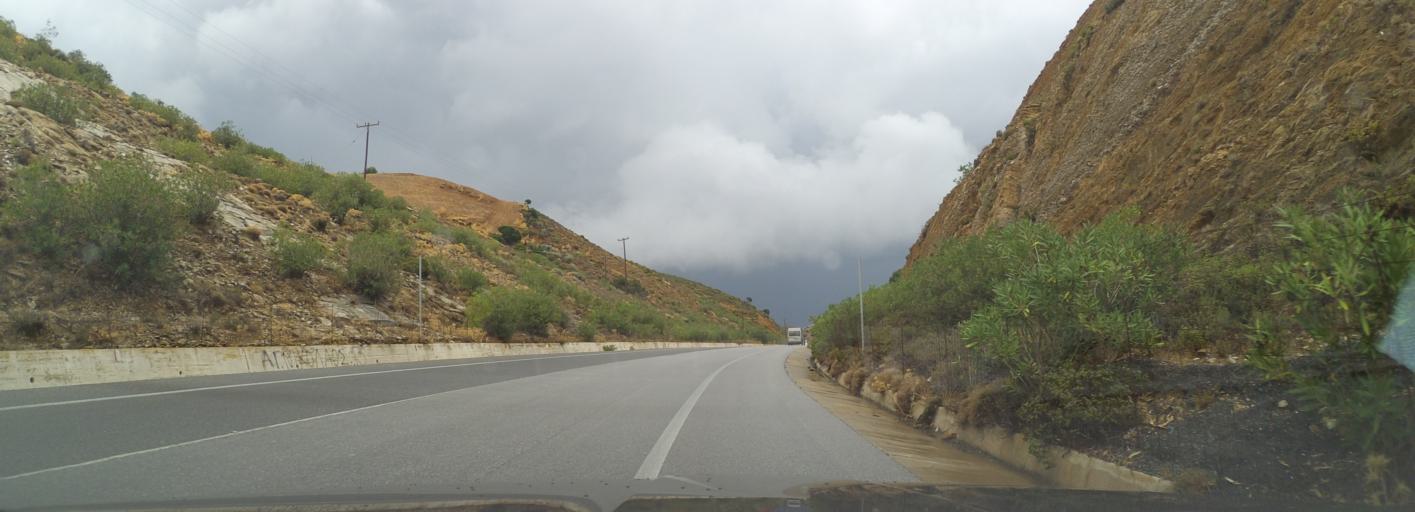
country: GR
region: Crete
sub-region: Nomos Rethymnis
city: Anogeia
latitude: 35.3906
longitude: 24.9295
